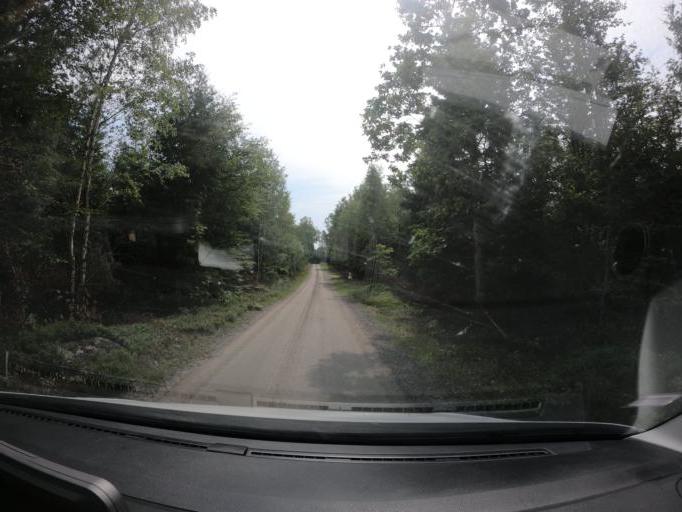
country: SE
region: Skane
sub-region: Hassleholms Kommun
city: Bjarnum
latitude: 56.2553
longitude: 13.6796
